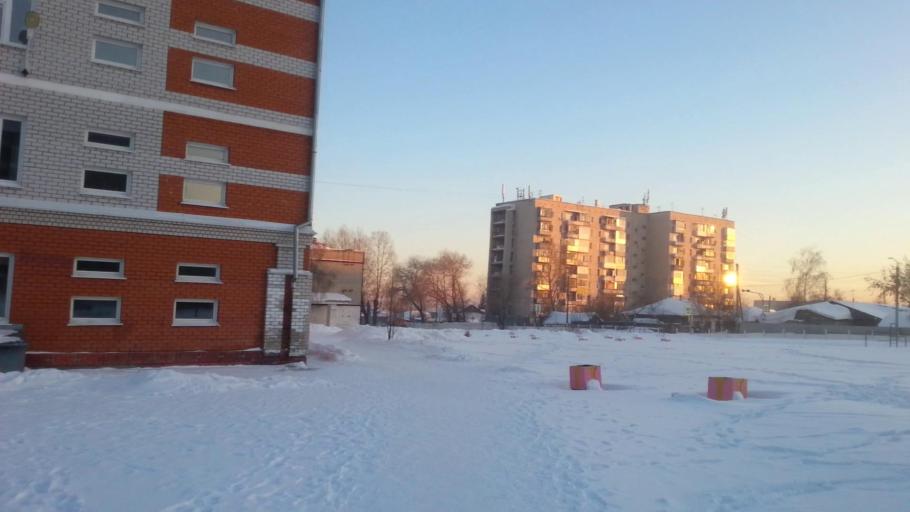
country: RU
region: Altai Krai
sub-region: Gorod Barnaulskiy
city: Barnaul
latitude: 53.3543
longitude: 83.7041
